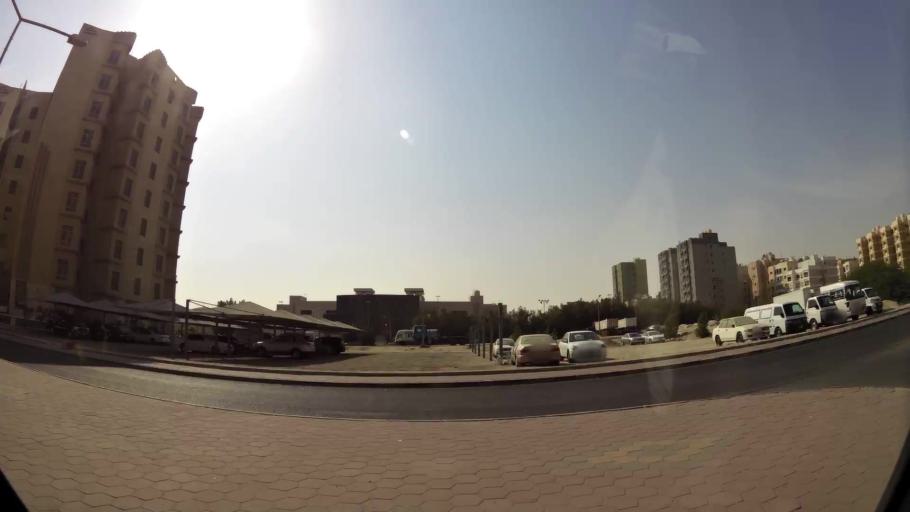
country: KW
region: Al Ahmadi
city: Al Mahbulah
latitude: 29.1356
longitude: 48.1223
